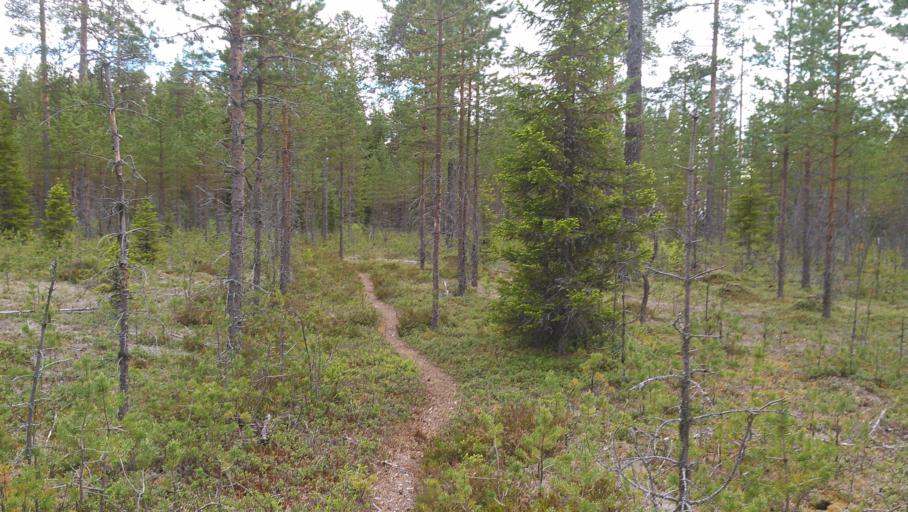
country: SE
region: Vaesterbotten
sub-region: Vannas Kommun
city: Vannasby
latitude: 64.0144
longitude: 19.9156
